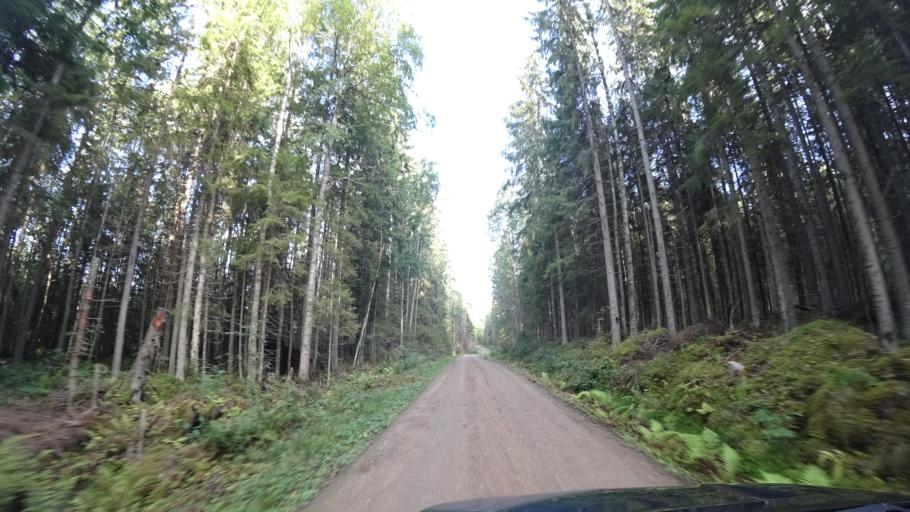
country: FI
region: Paijanne Tavastia
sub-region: Lahti
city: Auttoinen
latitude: 61.2201
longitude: 25.2046
